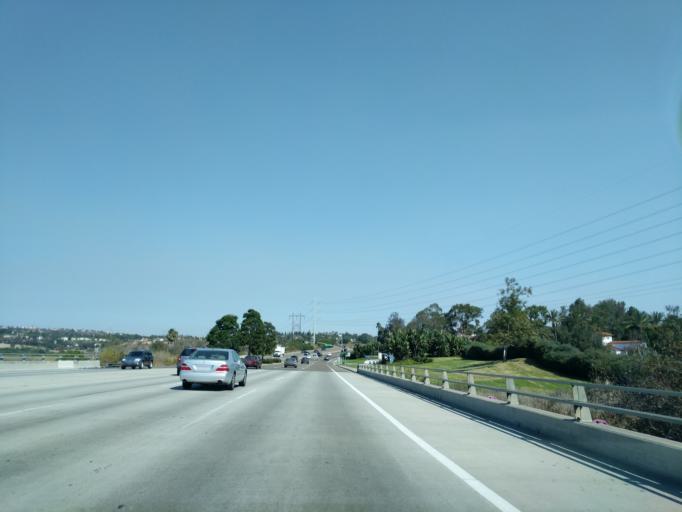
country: US
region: California
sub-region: San Diego County
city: Encinitas
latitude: 33.0877
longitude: -117.2690
